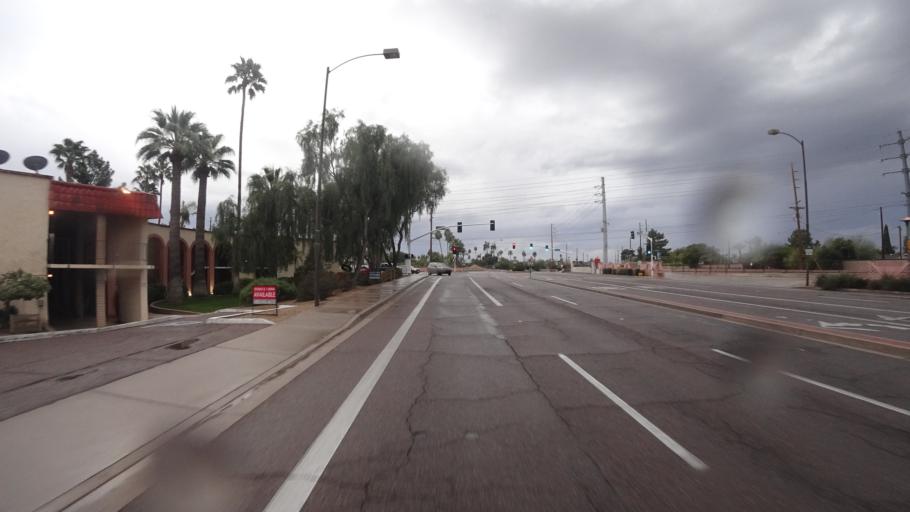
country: US
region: Arizona
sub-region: Maricopa County
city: Paradise Valley
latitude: 33.4905
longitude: -111.9423
